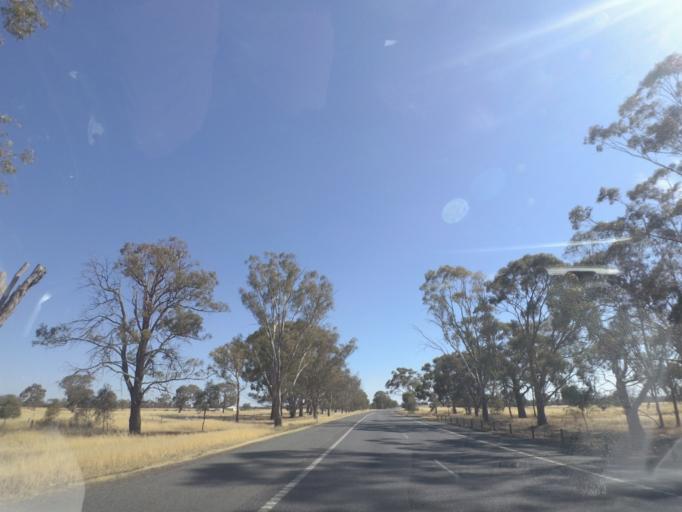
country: AU
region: Victoria
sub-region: Greater Shepparton
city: Shepparton
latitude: -36.6046
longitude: 145.3236
